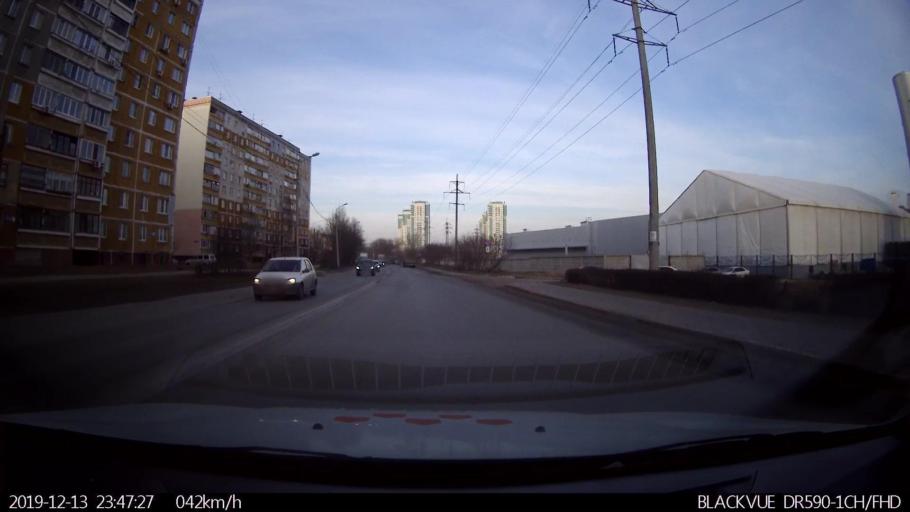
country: RU
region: Nizjnij Novgorod
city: Nizhniy Novgorod
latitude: 56.2941
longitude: 43.9523
